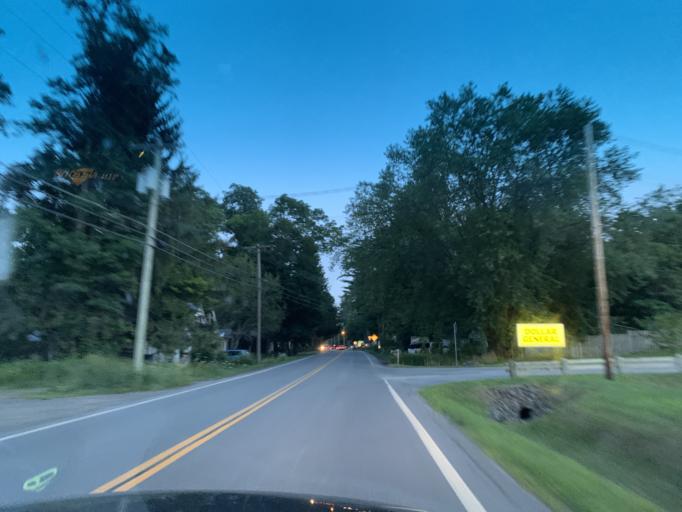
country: US
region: New York
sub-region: Chenango County
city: New Berlin
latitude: 42.6348
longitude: -75.3321
